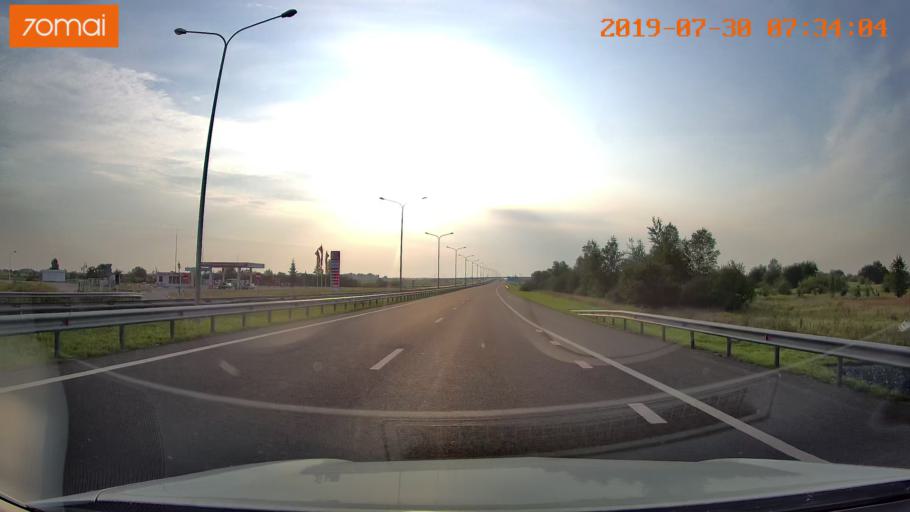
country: RU
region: Kaliningrad
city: Gvardeysk
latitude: 54.6713
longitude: 21.0624
